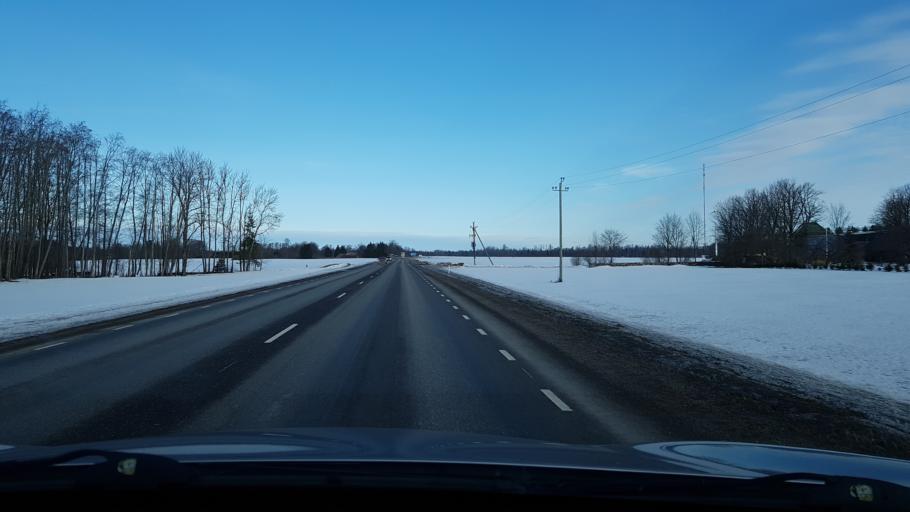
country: EE
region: Viljandimaa
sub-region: Viljandi linn
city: Viljandi
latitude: 58.4540
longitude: 25.5945
